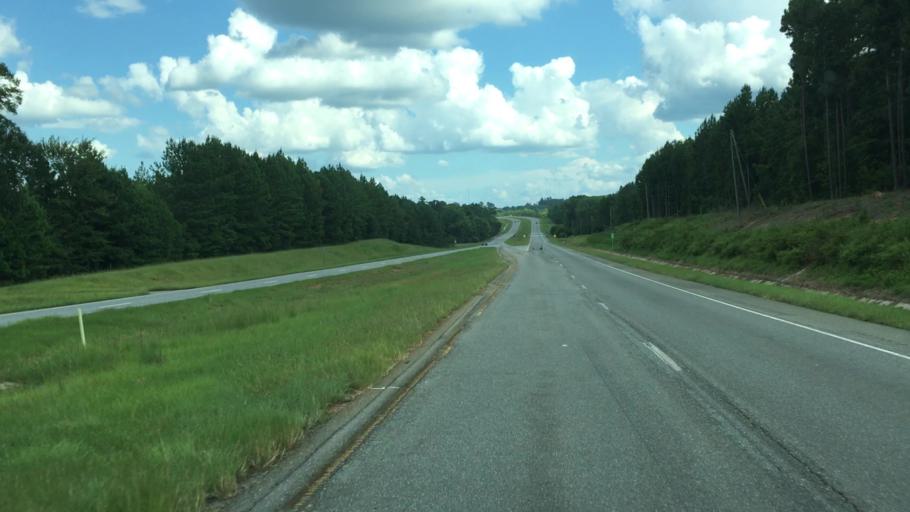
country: US
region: Georgia
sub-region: Wilkinson County
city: Irwinton
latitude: 32.7034
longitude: -83.1264
